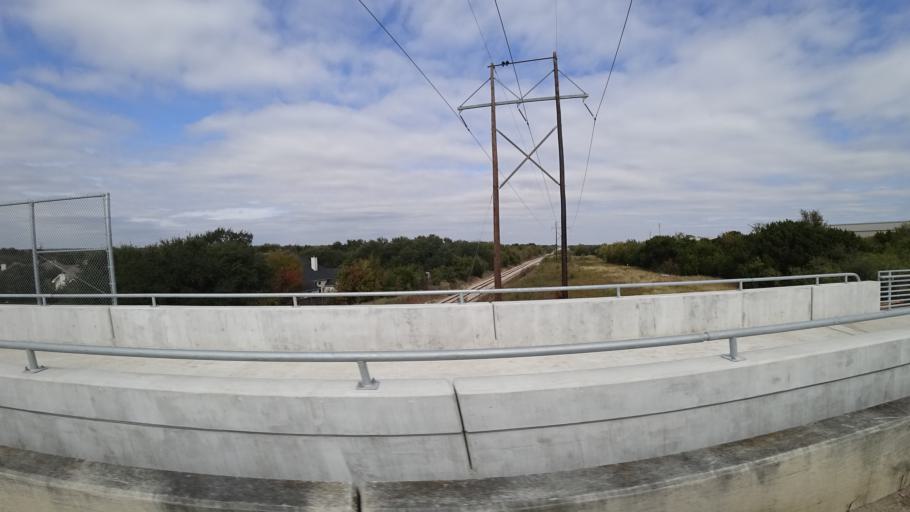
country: US
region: Texas
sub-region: Williamson County
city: Round Rock
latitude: 30.5350
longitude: -97.6988
